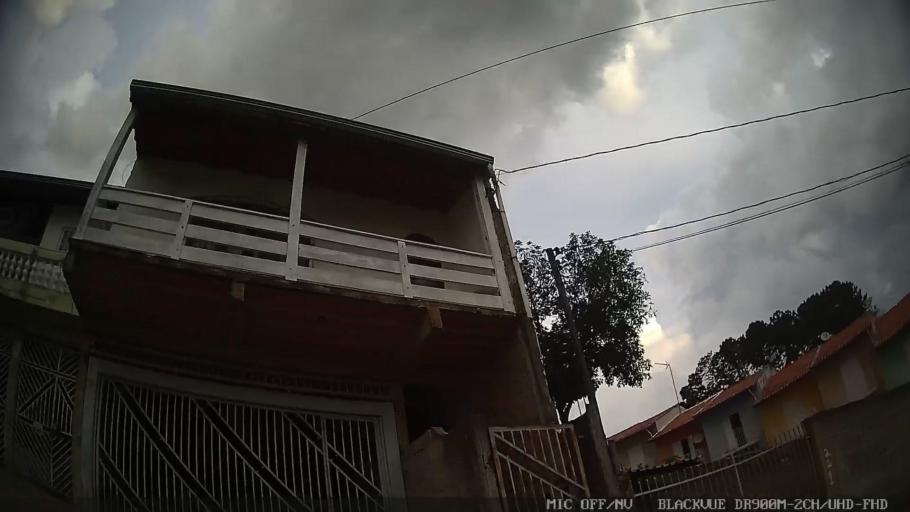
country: BR
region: Sao Paulo
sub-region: Braganca Paulista
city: Braganca Paulista
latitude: -22.9230
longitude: -46.5296
